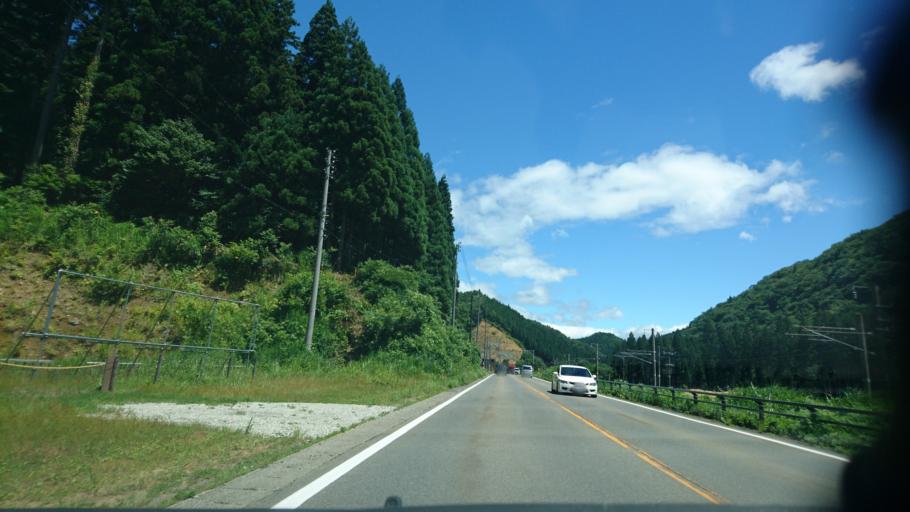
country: JP
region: Akita
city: Kakunodatemachi
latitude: 39.6481
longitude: 140.6653
